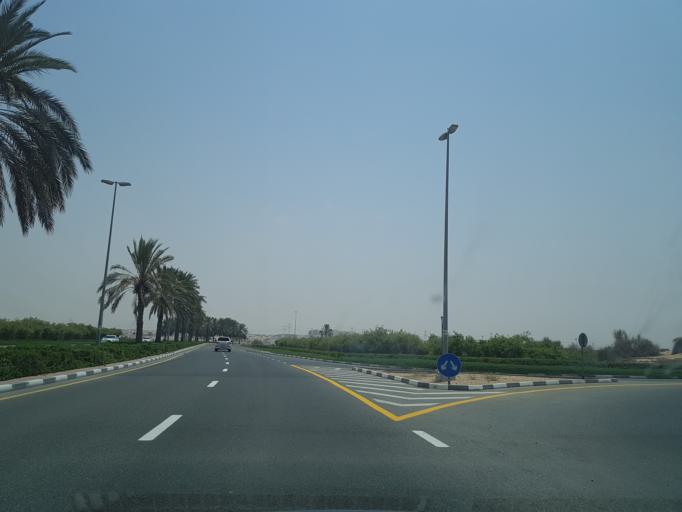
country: AE
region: Ash Shariqah
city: Sharjah
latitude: 25.1099
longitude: 55.3968
